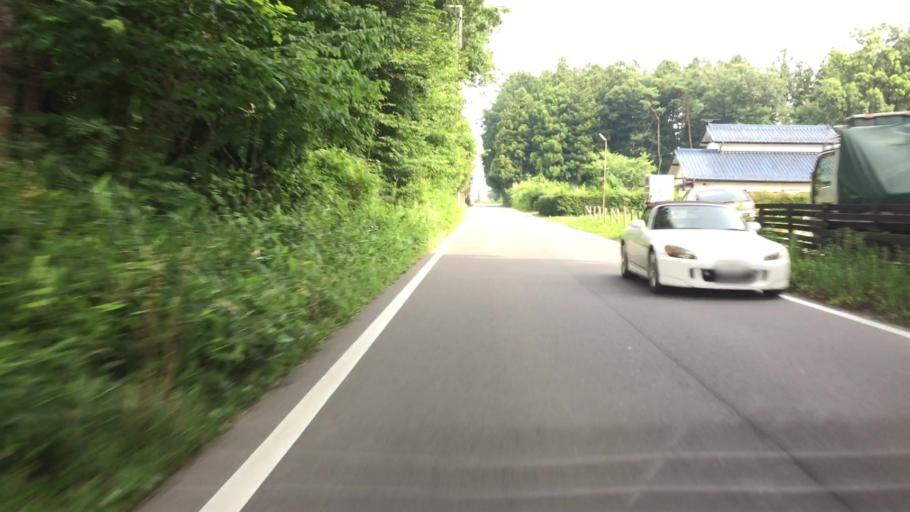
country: JP
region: Tochigi
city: Kuroiso
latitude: 36.9693
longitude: 139.9773
